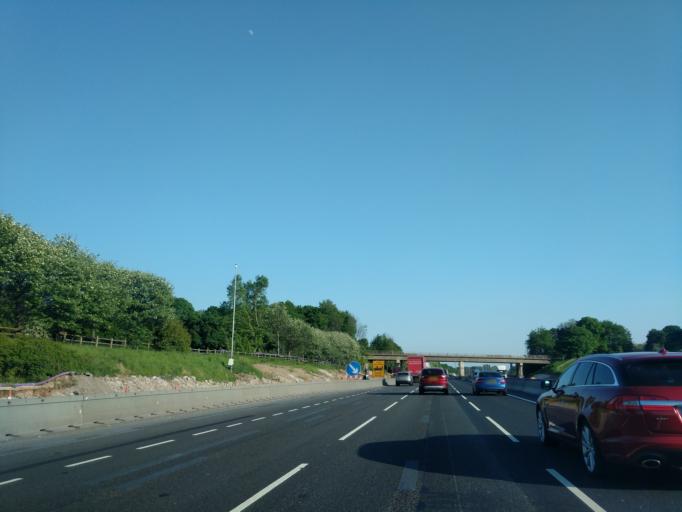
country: GB
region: England
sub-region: Cheshire East
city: Knutsford
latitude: 53.2980
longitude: -2.3996
